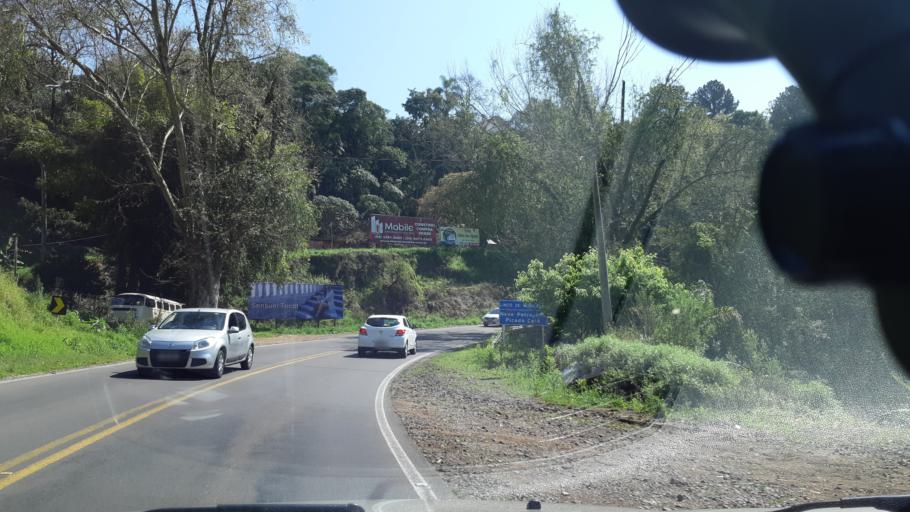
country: BR
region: Rio Grande do Sul
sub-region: Nova Petropolis
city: Nova Petropolis
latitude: -29.3987
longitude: -51.1275
